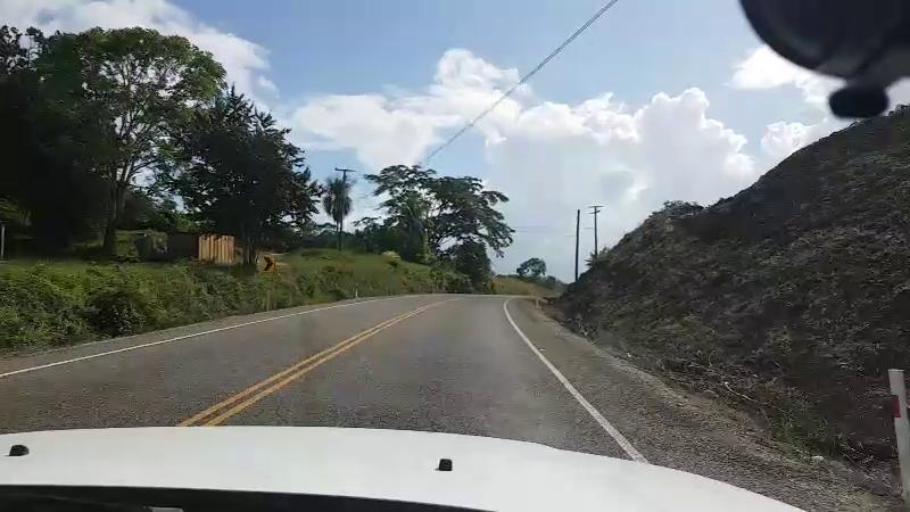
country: BZ
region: Cayo
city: Belmopan
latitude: 17.2308
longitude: -88.7795
